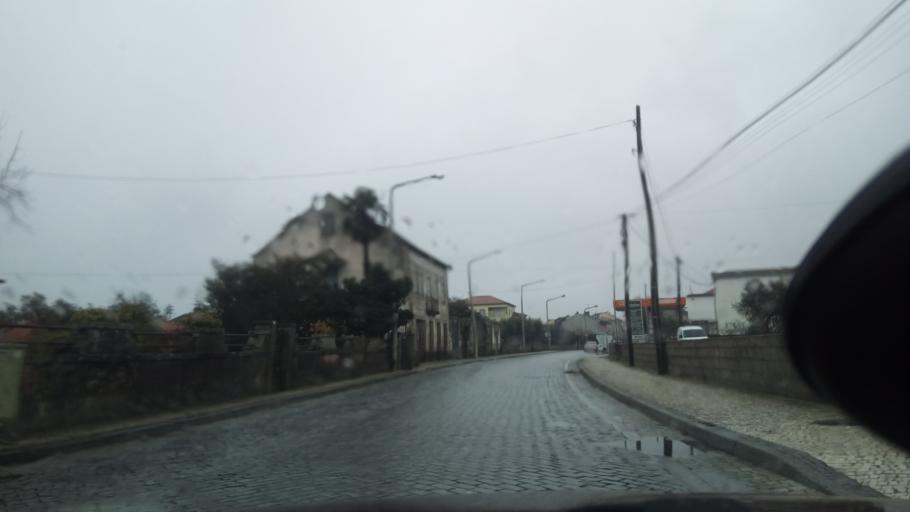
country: PT
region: Viseu
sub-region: Mangualde
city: Mangualde
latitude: 40.6044
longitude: -7.7527
